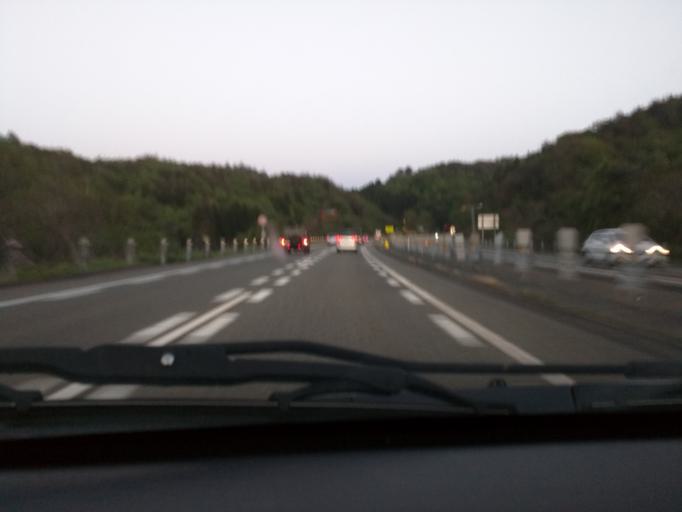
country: JP
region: Niigata
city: Kashiwazaki
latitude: 37.3461
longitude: 138.5119
